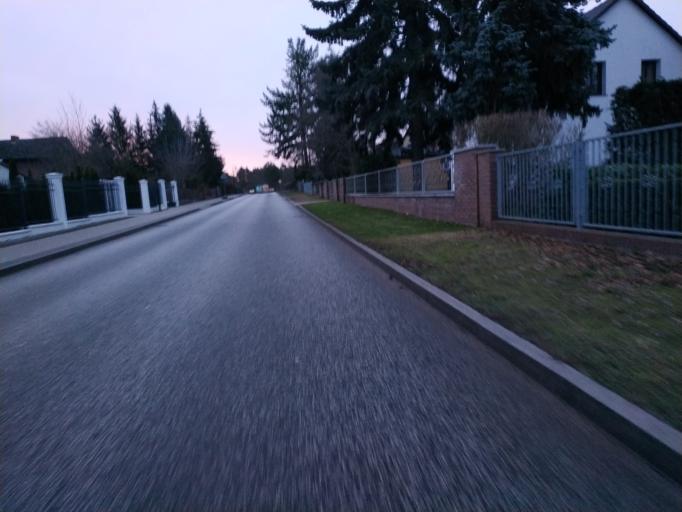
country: DE
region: Brandenburg
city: Petershagen
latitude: 52.5335
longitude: 13.8218
